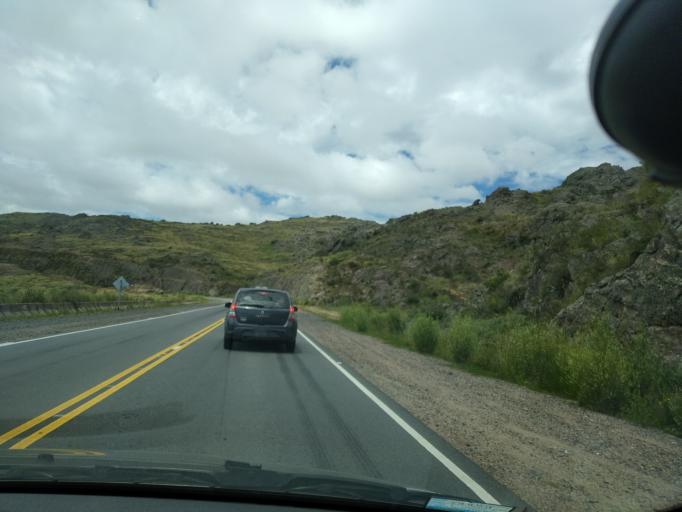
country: AR
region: Cordoba
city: Cuesta Blanca
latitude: -31.6024
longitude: -64.7029
